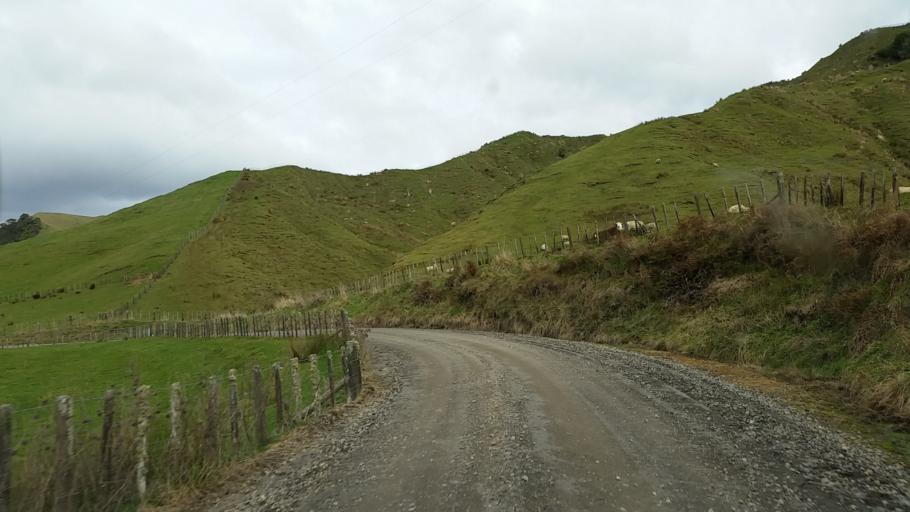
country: NZ
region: Taranaki
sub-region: New Plymouth District
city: Waitara
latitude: -39.1654
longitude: 174.5990
